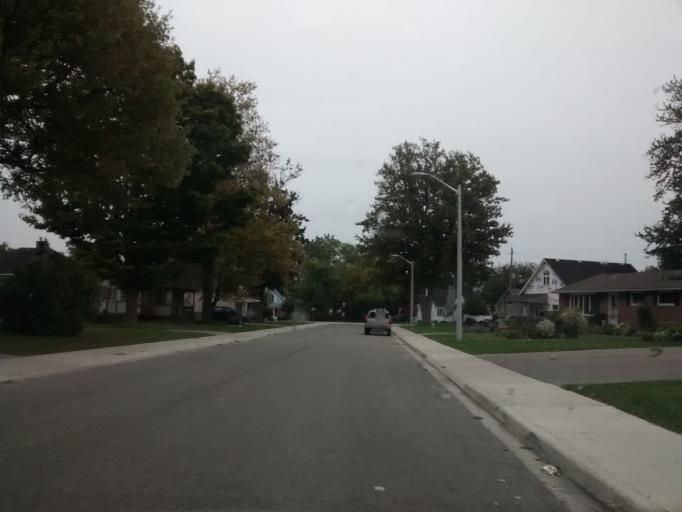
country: CA
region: Ontario
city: Welland
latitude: 42.9043
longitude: -79.6093
